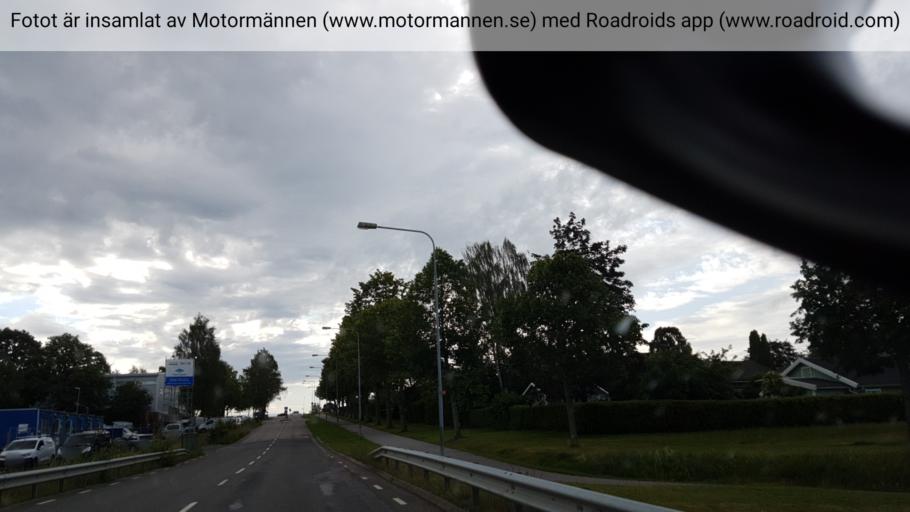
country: SE
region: Vaestra Goetaland
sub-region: Gotene Kommun
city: Kallby
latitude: 58.5086
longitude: 13.3065
